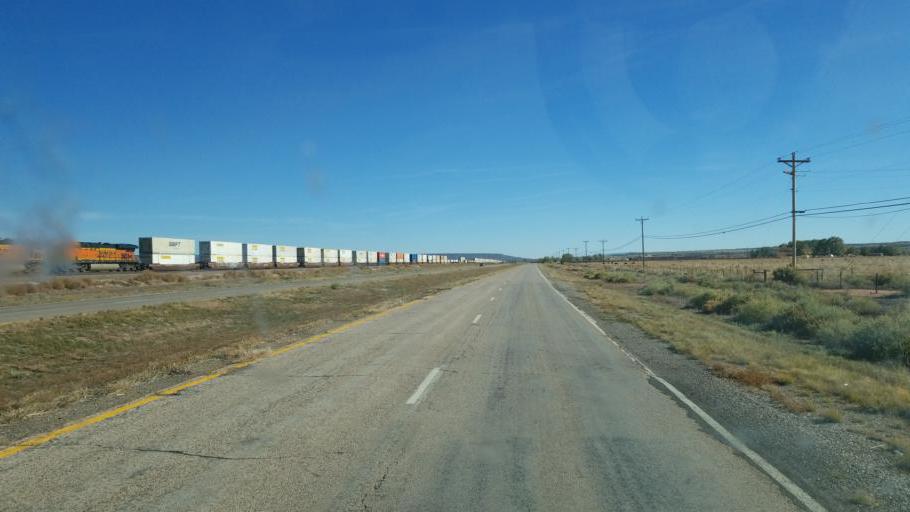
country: US
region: New Mexico
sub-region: Cibola County
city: Milan
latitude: 35.2623
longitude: -107.9699
